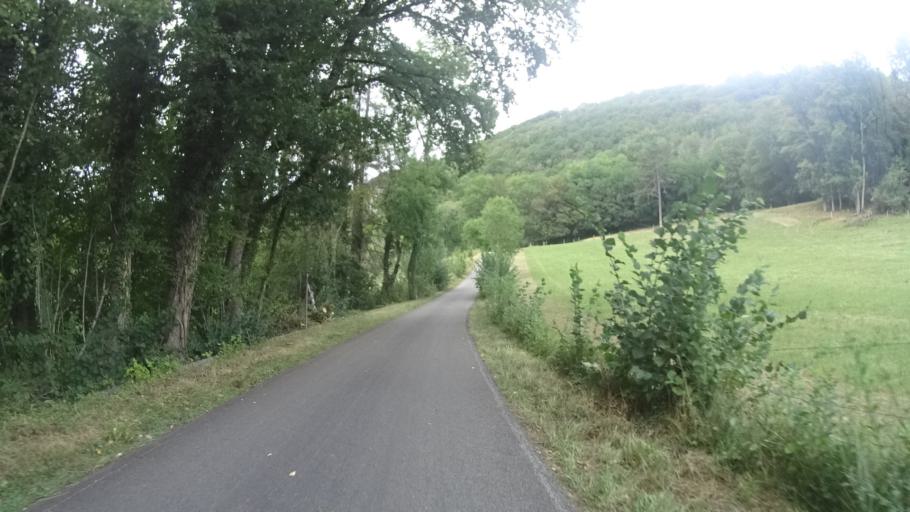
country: FR
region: Franche-Comte
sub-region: Departement du Doubs
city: Baume-les-Dames
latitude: 47.3365
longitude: 6.3469
